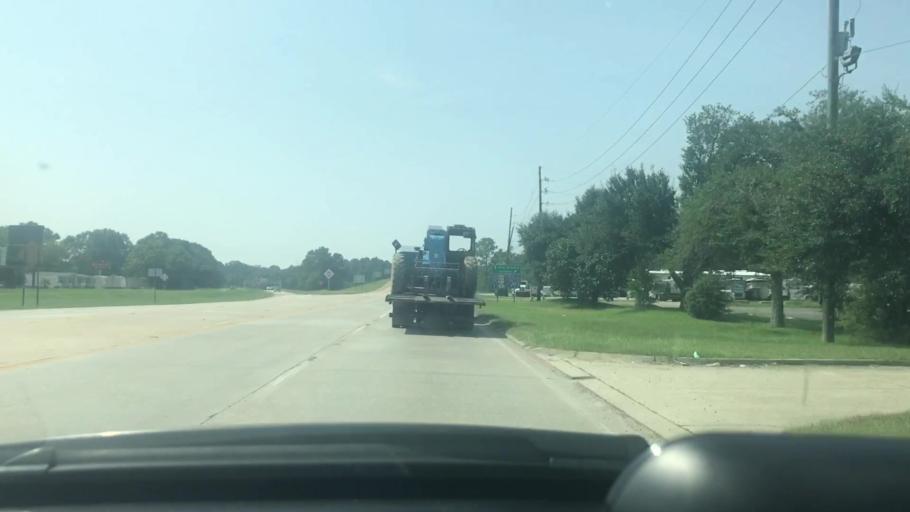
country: US
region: Louisiana
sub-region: Tangipahoa Parish
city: Hammond
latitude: 30.4739
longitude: -90.4827
